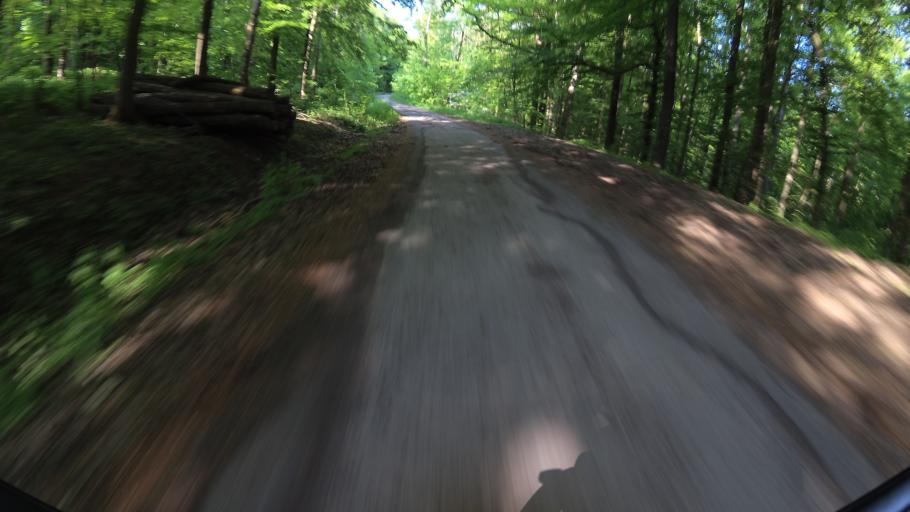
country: DE
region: Saarland
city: Marpingen
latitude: 49.4151
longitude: 7.0414
